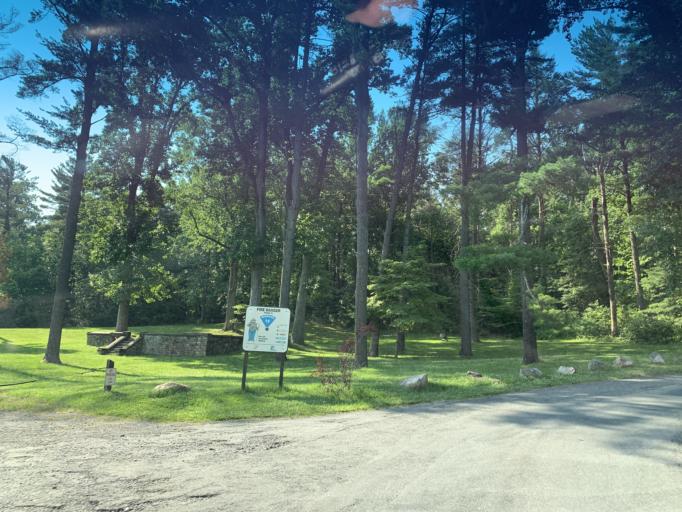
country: US
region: Maryland
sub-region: Frederick County
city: Urbana
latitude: 39.2527
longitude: -77.3941
